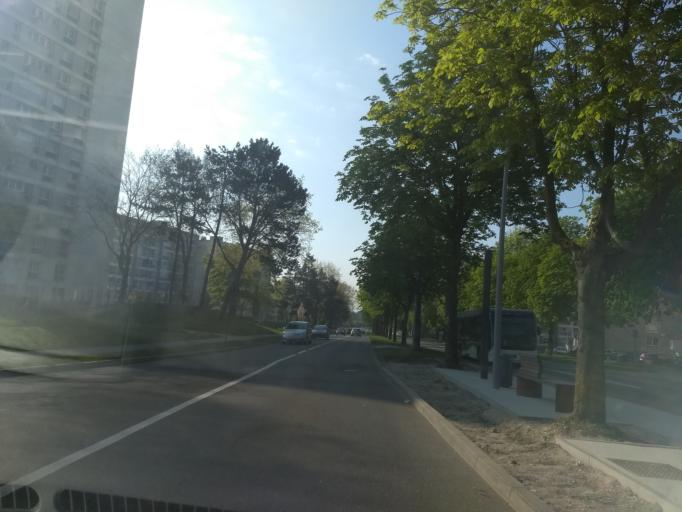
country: FR
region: Picardie
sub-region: Departement de la Somme
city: Rivery
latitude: 49.9105
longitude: 2.3164
